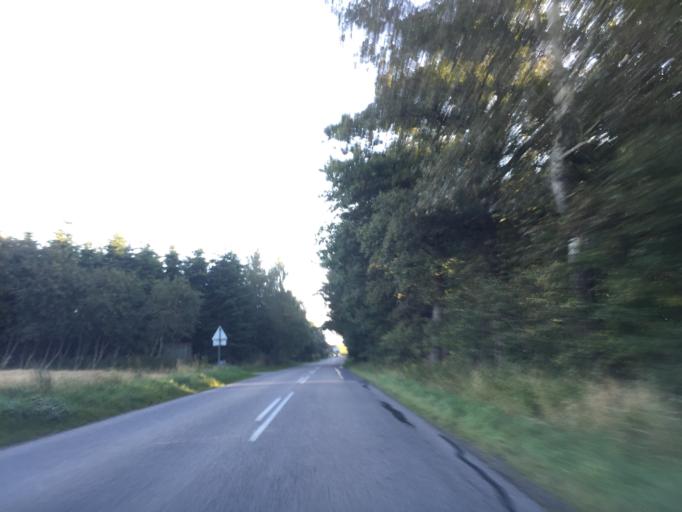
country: DK
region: Central Jutland
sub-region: Viborg Kommune
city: Bjerringbro
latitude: 56.3291
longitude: 9.6307
